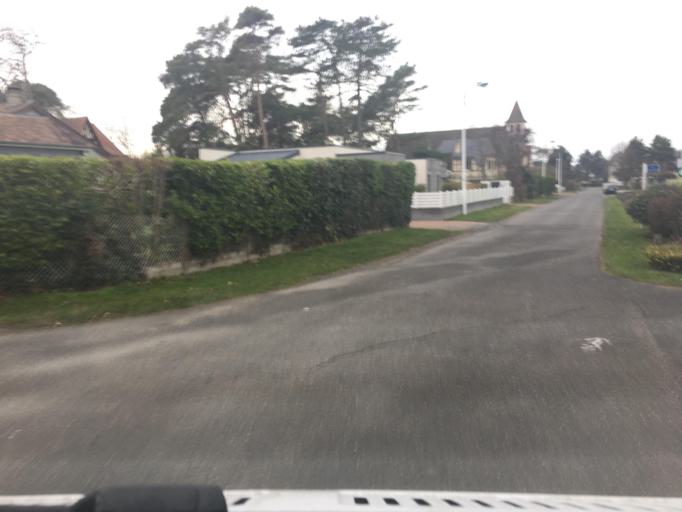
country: FR
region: Lower Normandy
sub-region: Departement du Calvados
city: Merville-Franceville-Plage
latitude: 49.2808
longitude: -0.2052
